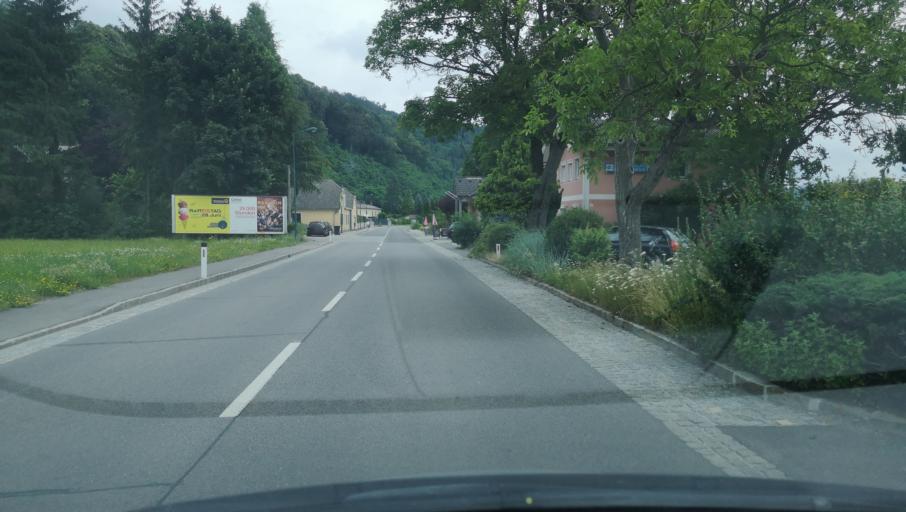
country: AT
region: Lower Austria
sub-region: Politischer Bezirk Melk
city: Ybbs an der Donau
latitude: 48.1989
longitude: 15.1079
